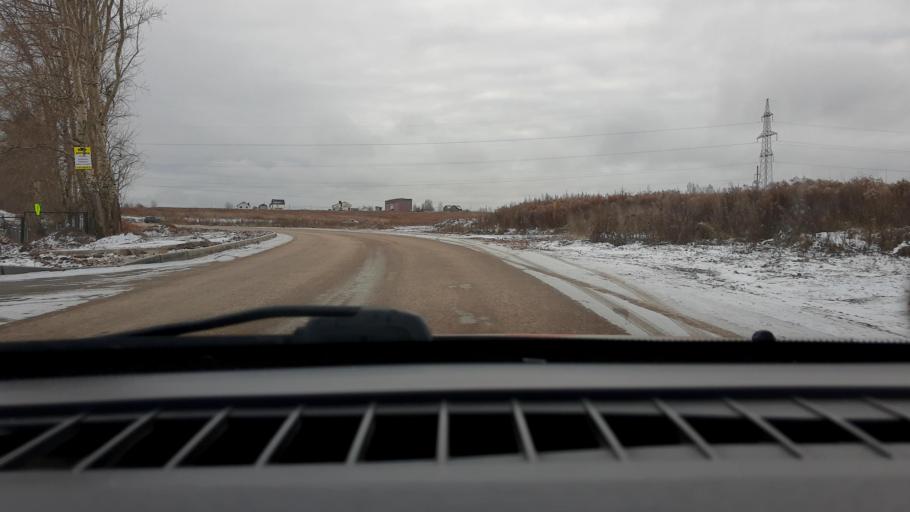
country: RU
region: Nizjnij Novgorod
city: Afonino
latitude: 56.2716
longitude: 44.0433
